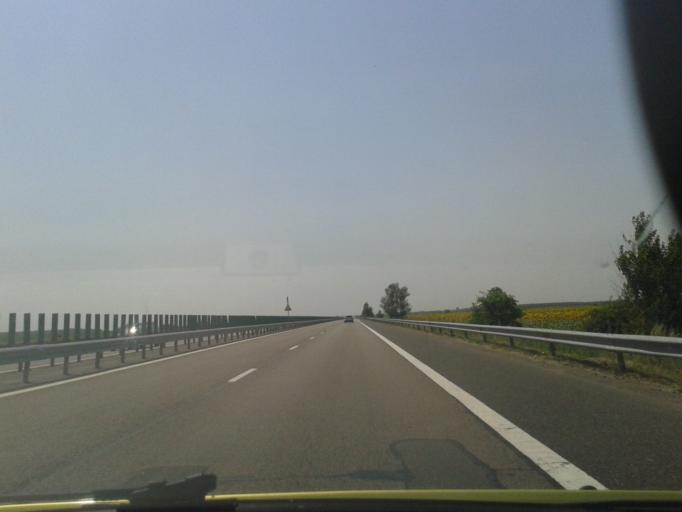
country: RO
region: Calarasi
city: Voda Dragos
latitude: 44.4285
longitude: 27.1035
